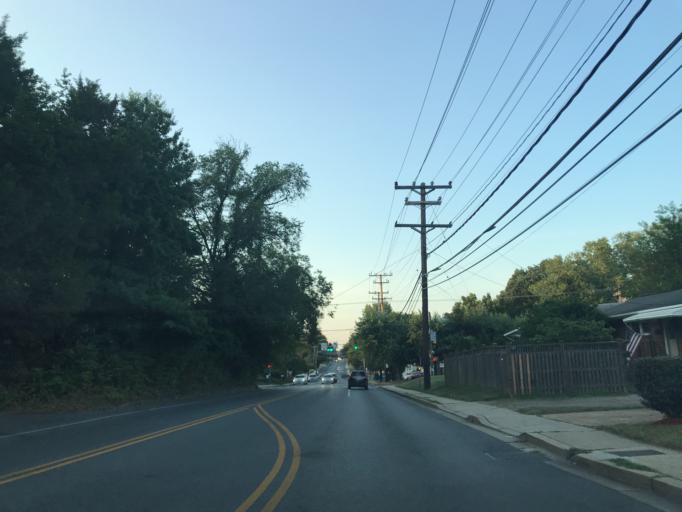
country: US
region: Maryland
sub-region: Anne Arundel County
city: Hillsmere Shores
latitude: 38.9591
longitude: -76.4913
